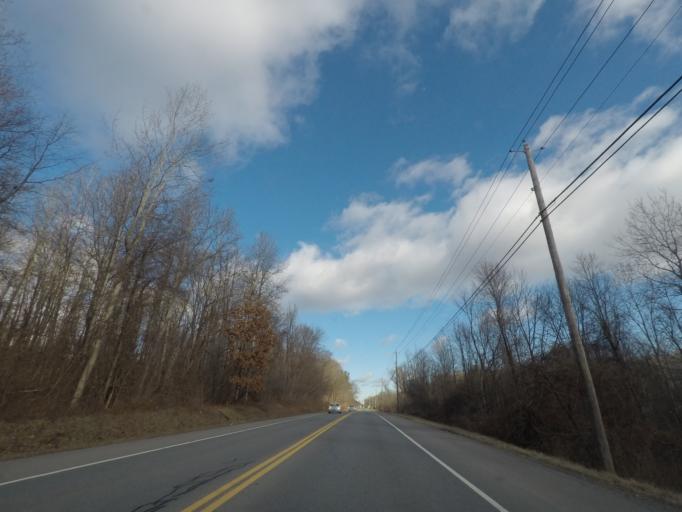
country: US
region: New York
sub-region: Saratoga County
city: Waterford
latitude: 42.7679
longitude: -73.6607
